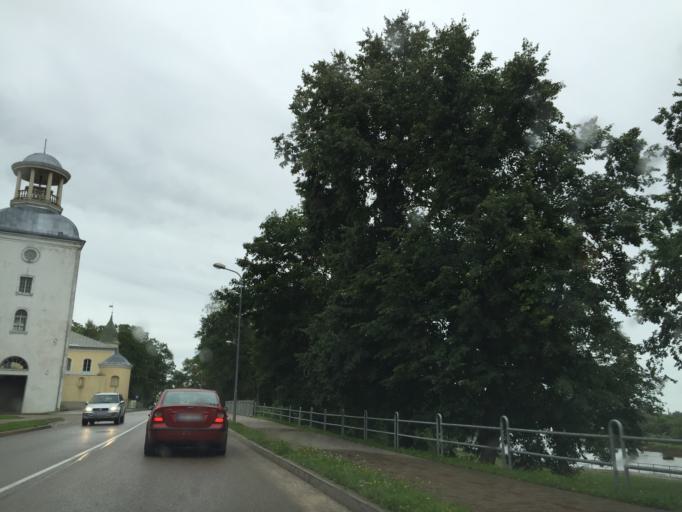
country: LV
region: Jekabpils Rajons
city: Jekabpils
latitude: 56.5119
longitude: 25.8576
